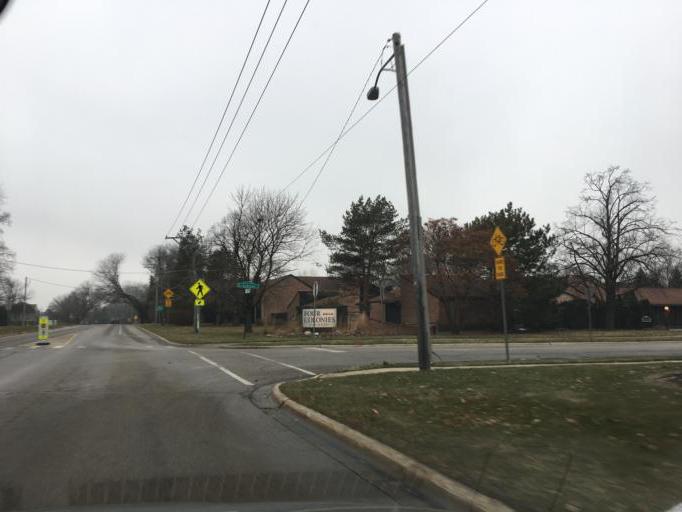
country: US
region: Illinois
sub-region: McHenry County
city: Lakewood
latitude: 42.2190
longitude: -88.3452
